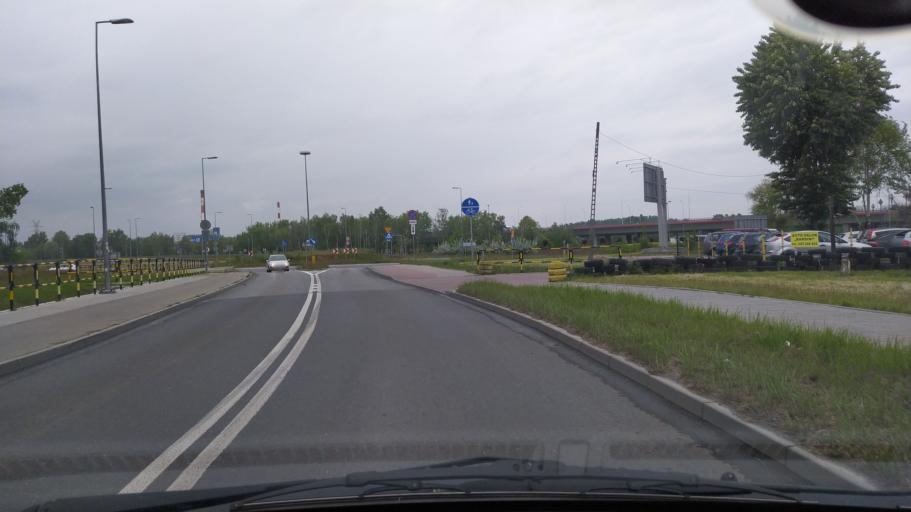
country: PL
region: Silesian Voivodeship
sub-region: Gliwice
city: Gliwice
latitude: 50.2823
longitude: 18.7155
